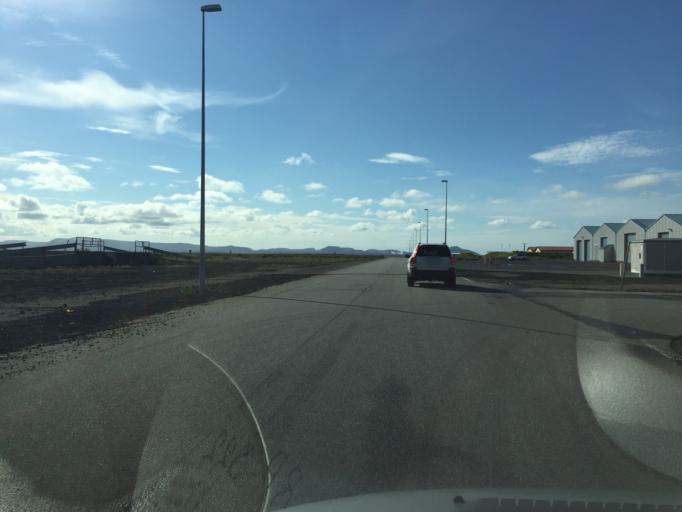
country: IS
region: Southern Peninsula
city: Reykjanesbaer
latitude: 63.9661
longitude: -22.5751
